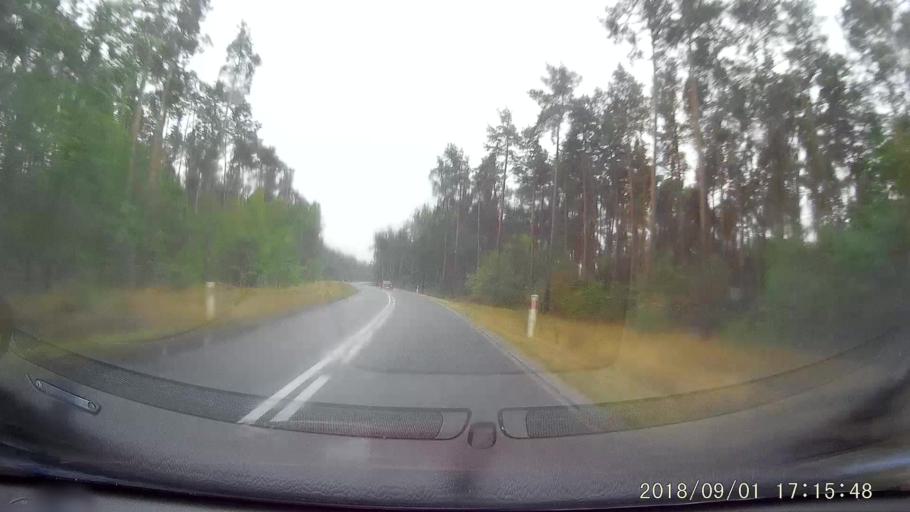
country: PL
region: Lubusz
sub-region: Powiat zielonogorski
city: Nowogrod Bobrzanski
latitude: 51.7709
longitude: 15.2657
